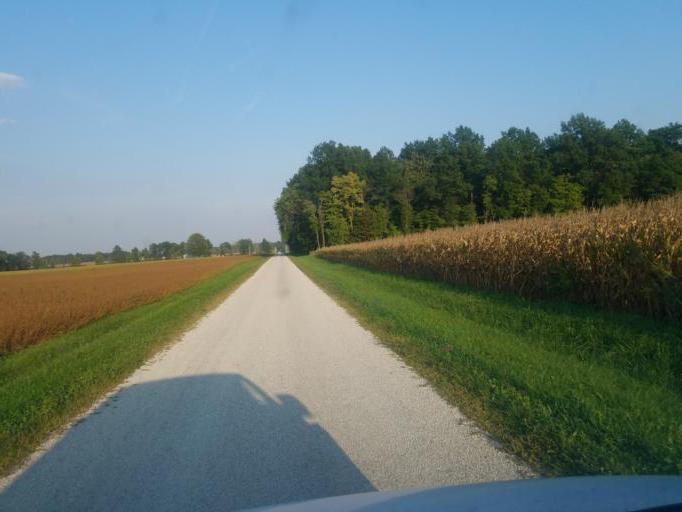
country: US
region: Ohio
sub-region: Crawford County
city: Bucyrus
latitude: 40.9068
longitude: -82.9155
